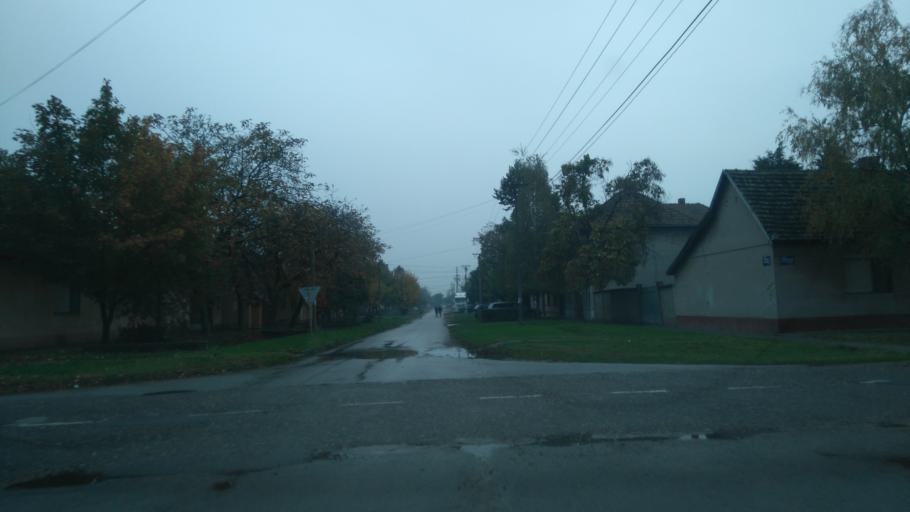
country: RS
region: Autonomna Pokrajina Vojvodina
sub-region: Juznobacki Okrug
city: Becej
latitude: 45.6081
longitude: 20.0336
